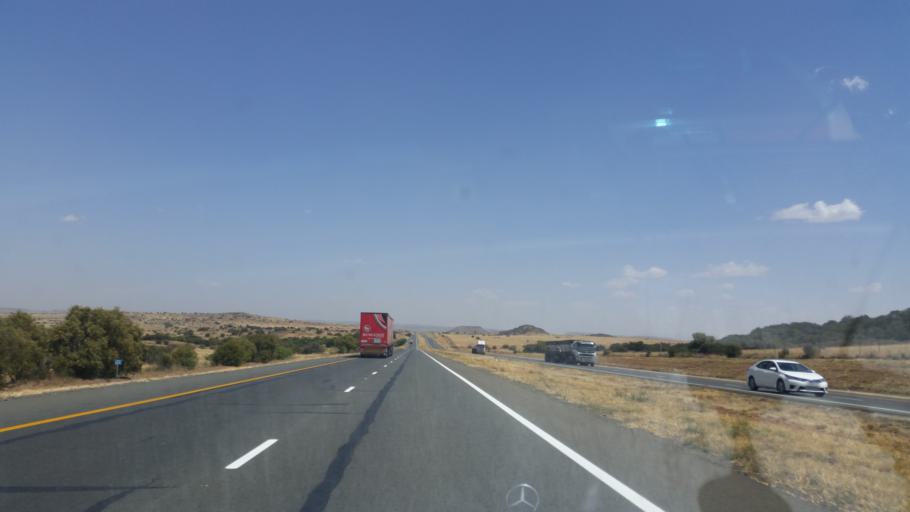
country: ZA
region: Orange Free State
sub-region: Lejweleputswa District Municipality
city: Brandfort
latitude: -28.9194
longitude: 26.4432
